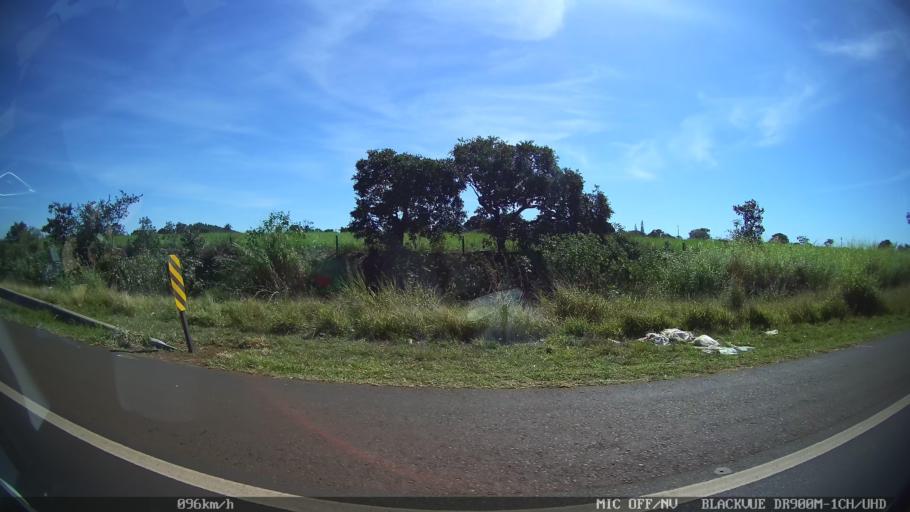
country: BR
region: Sao Paulo
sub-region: Franca
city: Franca
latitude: -20.5486
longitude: -47.4819
